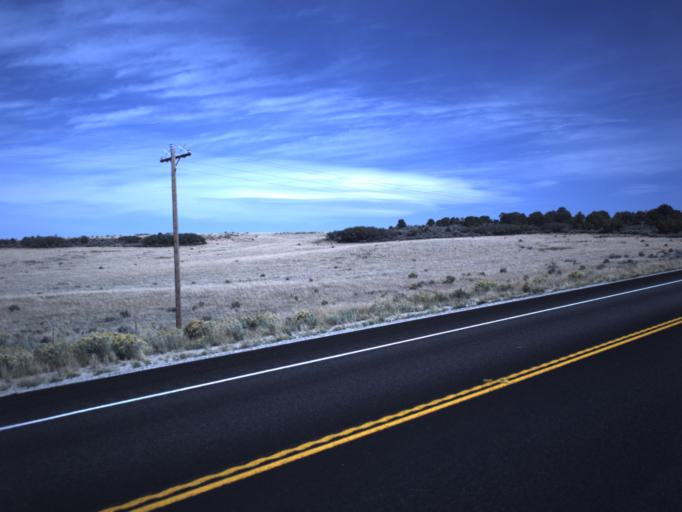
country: US
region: Utah
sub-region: San Juan County
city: Monticello
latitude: 37.8661
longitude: -109.2341
